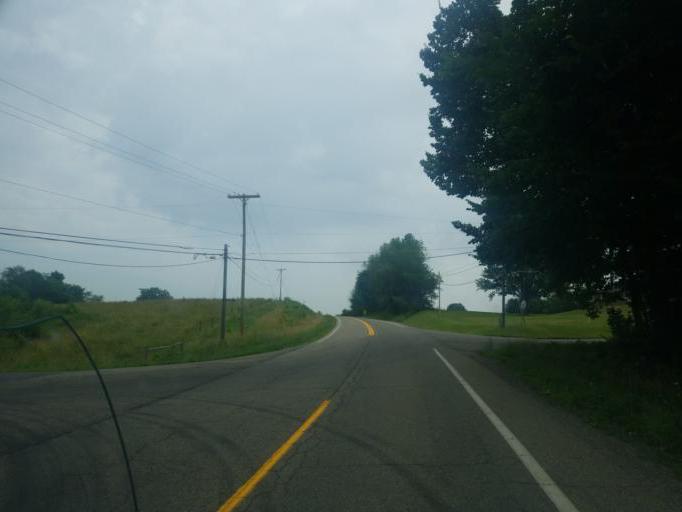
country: US
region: Ohio
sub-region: Columbiana County
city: Salem
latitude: 40.7774
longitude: -80.9305
